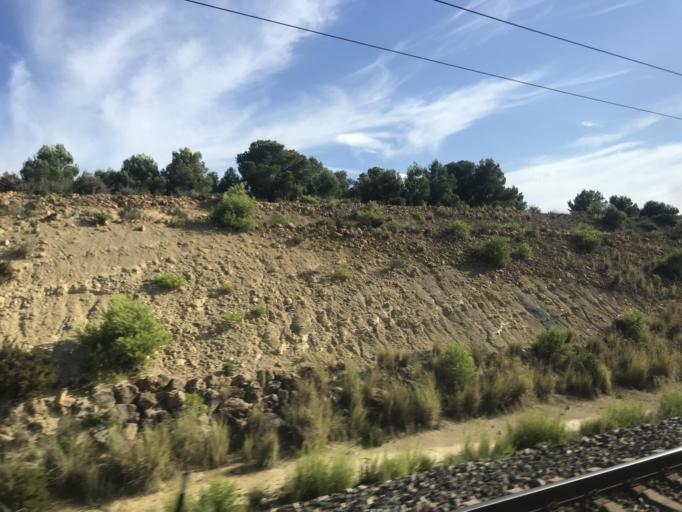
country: ES
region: Catalonia
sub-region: Provincia de Tarragona
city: El Perello
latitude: 40.8509
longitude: 0.7597
